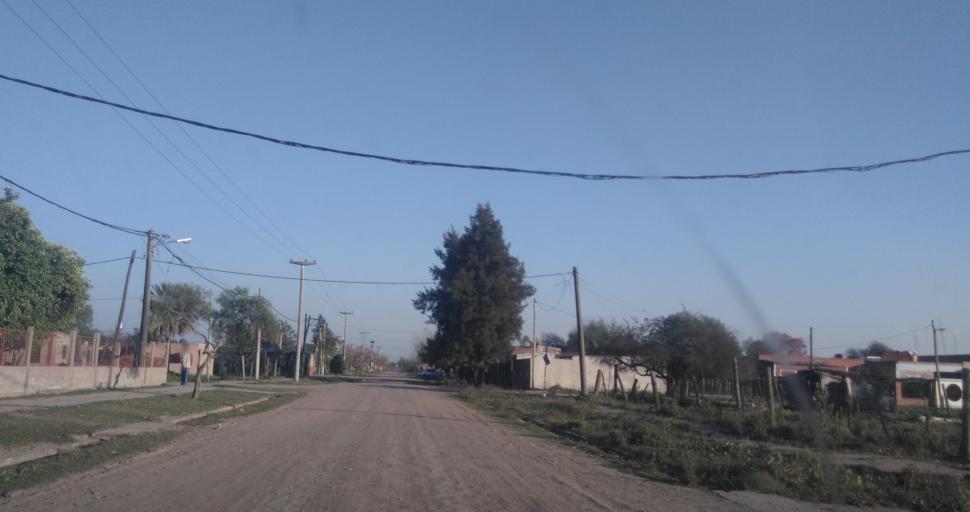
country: AR
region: Chaco
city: Resistencia
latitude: -27.4874
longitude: -58.9998
